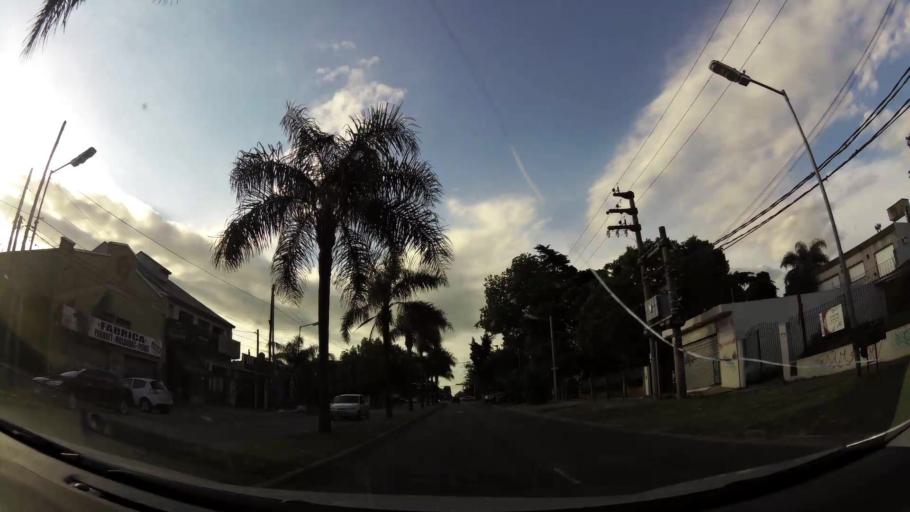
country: AR
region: Buenos Aires
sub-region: Partido de Tigre
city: Tigre
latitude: -34.4647
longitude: -58.6265
